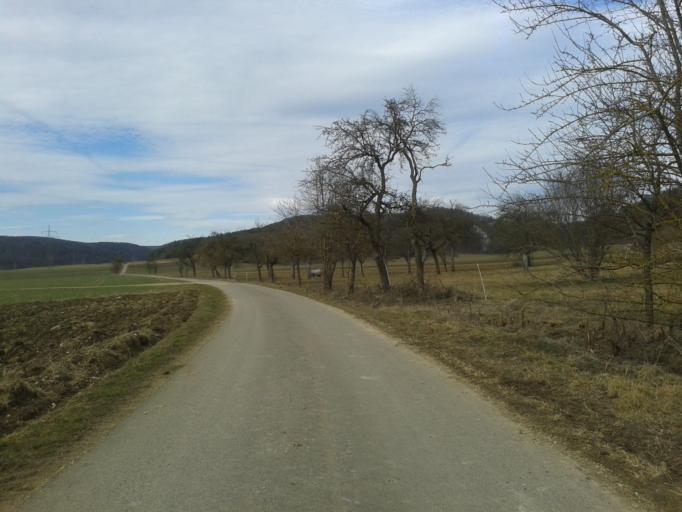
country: DE
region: Baden-Wuerttemberg
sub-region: Tuebingen Region
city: Altheim
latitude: 48.3503
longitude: 9.7530
